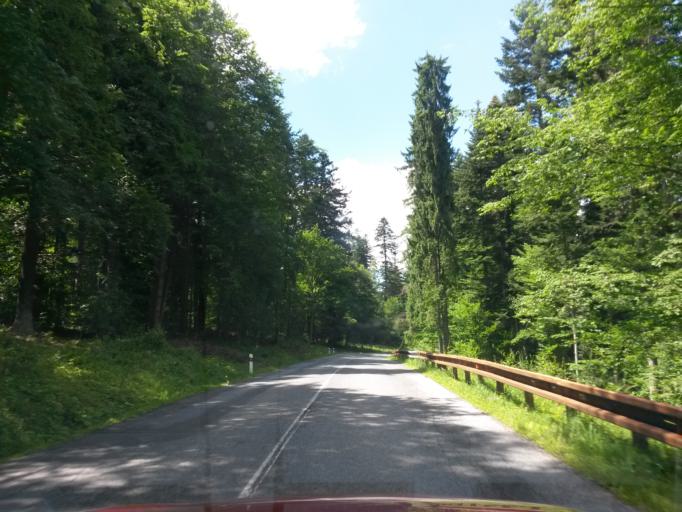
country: SK
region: Kosicky
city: Medzev
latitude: 48.7917
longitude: 20.7526
